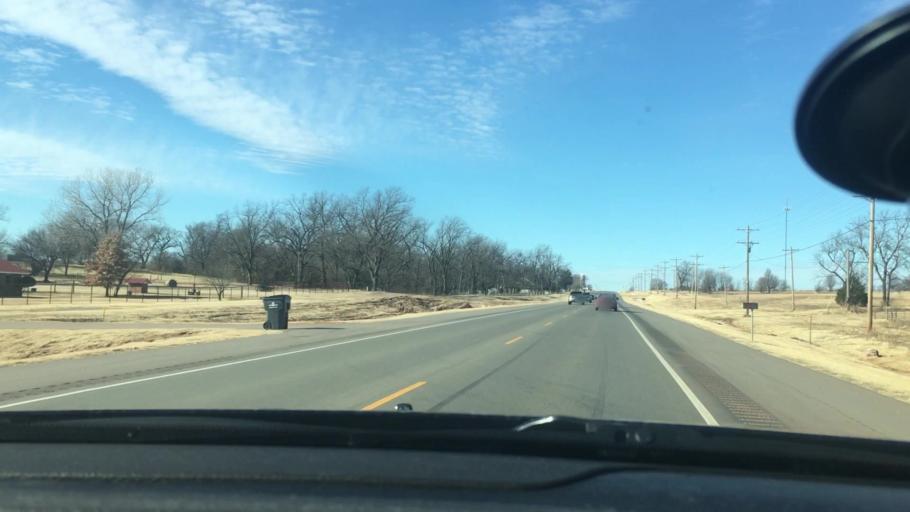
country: US
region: Oklahoma
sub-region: Cleveland County
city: Lexington
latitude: 35.0149
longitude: -97.2565
